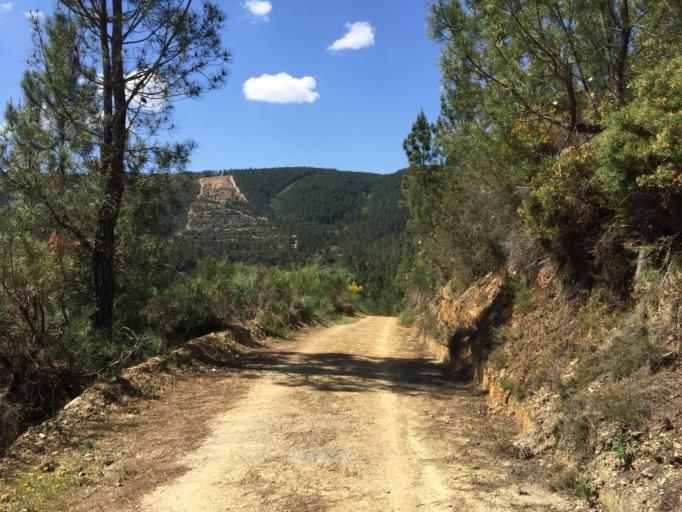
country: PT
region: Coimbra
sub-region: Pampilhosa da Serra
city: Pampilhosa da Serra
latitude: 40.0735
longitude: -7.7736
